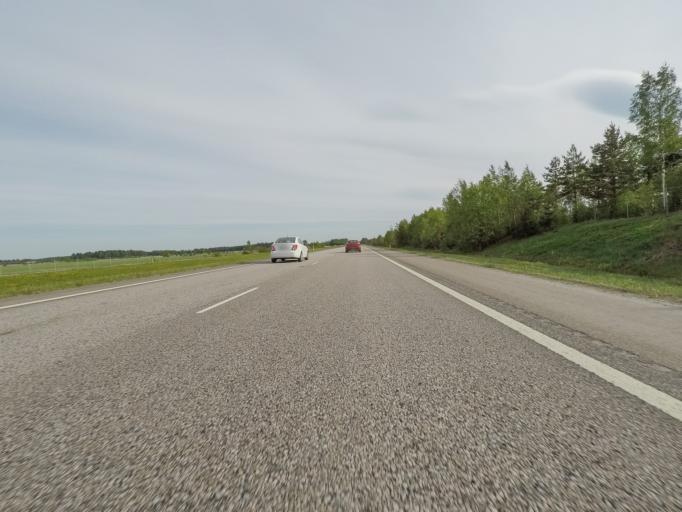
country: FI
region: Uusimaa
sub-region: Helsinki
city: Nurmijaervi
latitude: 60.5311
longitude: 24.8419
